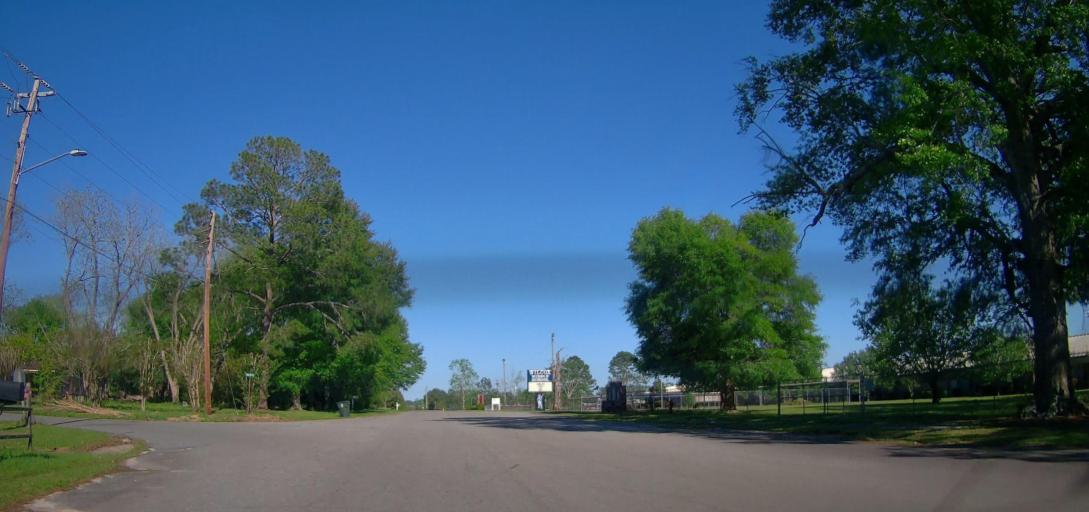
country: US
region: Georgia
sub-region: Wilcox County
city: Rochelle
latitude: 31.9440
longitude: -83.4554
